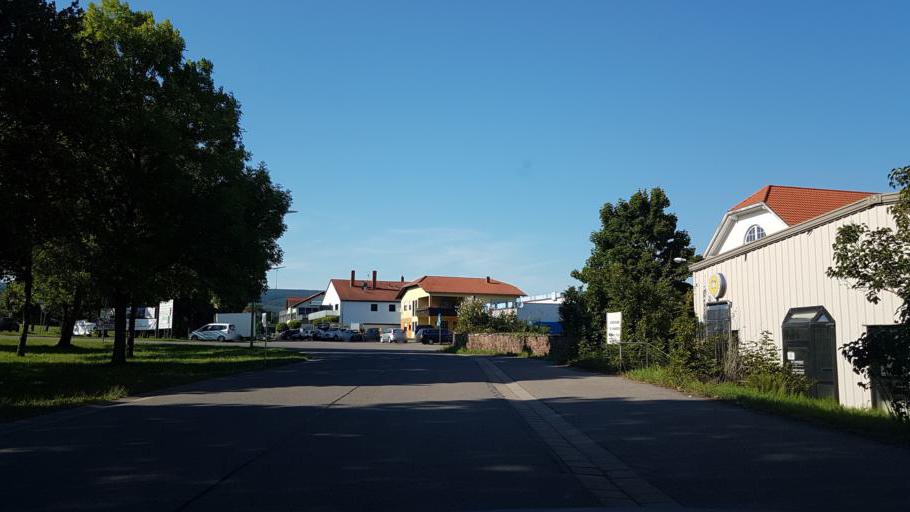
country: DE
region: Saarland
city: Weiskirchen
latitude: 49.5476
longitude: 6.8307
